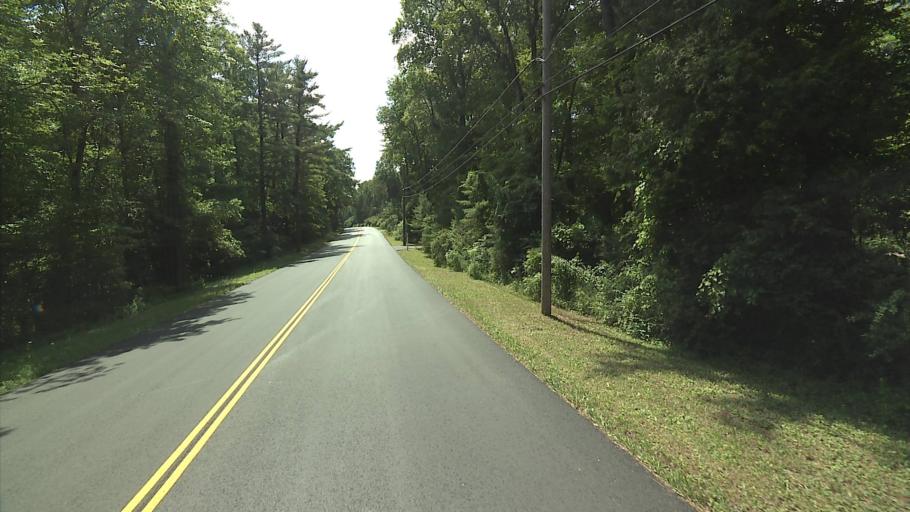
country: US
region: Connecticut
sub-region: Litchfield County
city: Canaan
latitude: 41.9948
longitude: -73.3608
